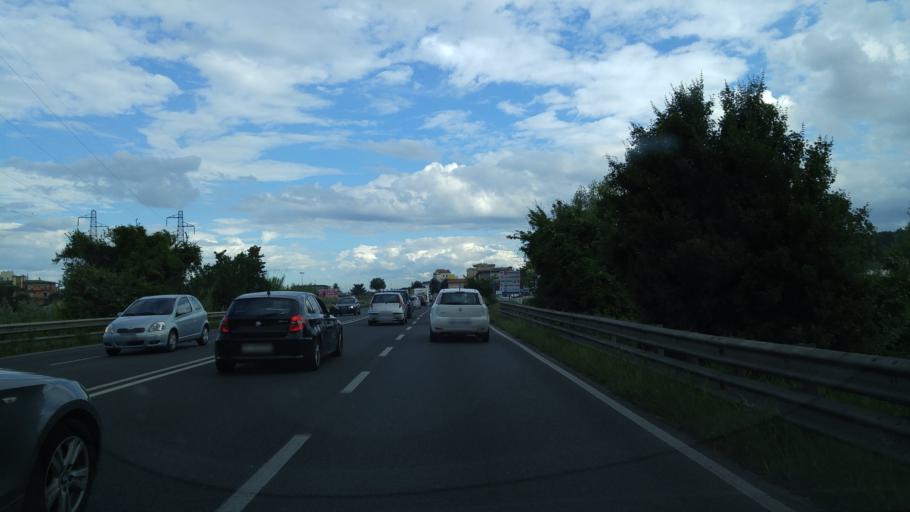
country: IT
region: Emilia-Romagna
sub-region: Provincia di Rimini
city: Rimini
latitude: 44.0493
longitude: 12.5491
